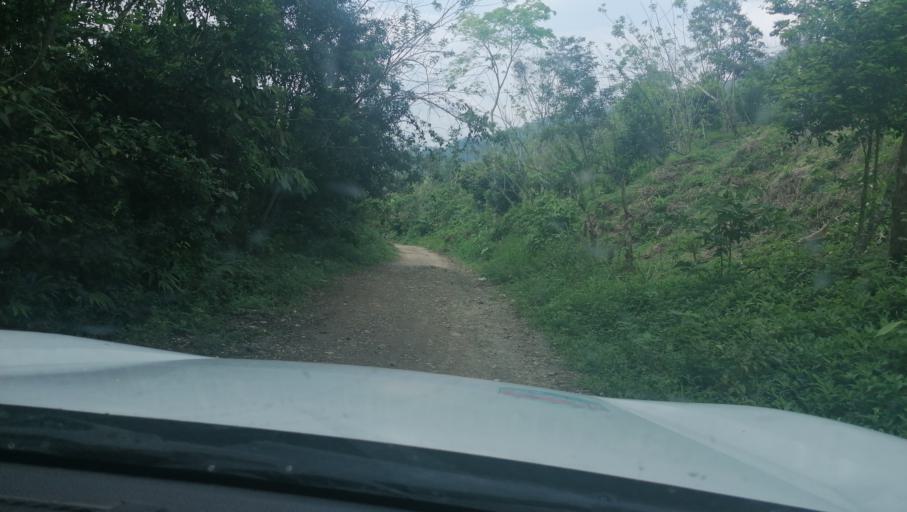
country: MX
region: Chiapas
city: Ostuacan
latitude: 17.3605
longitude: -93.3245
